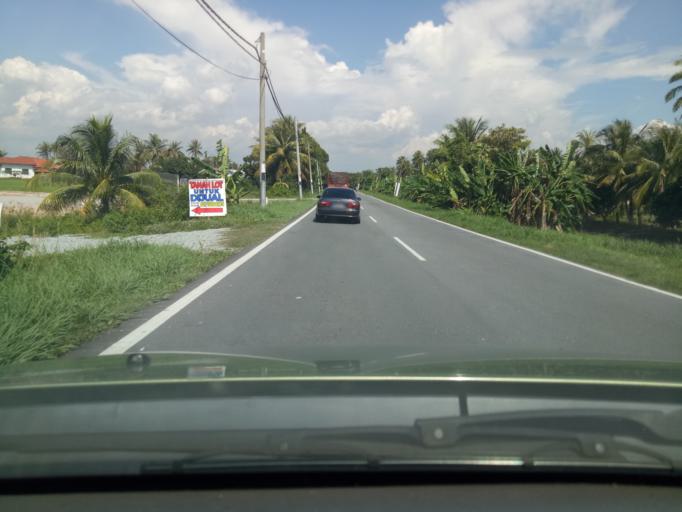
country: MY
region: Kedah
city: Alor Setar
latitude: 5.9715
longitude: 100.4160
